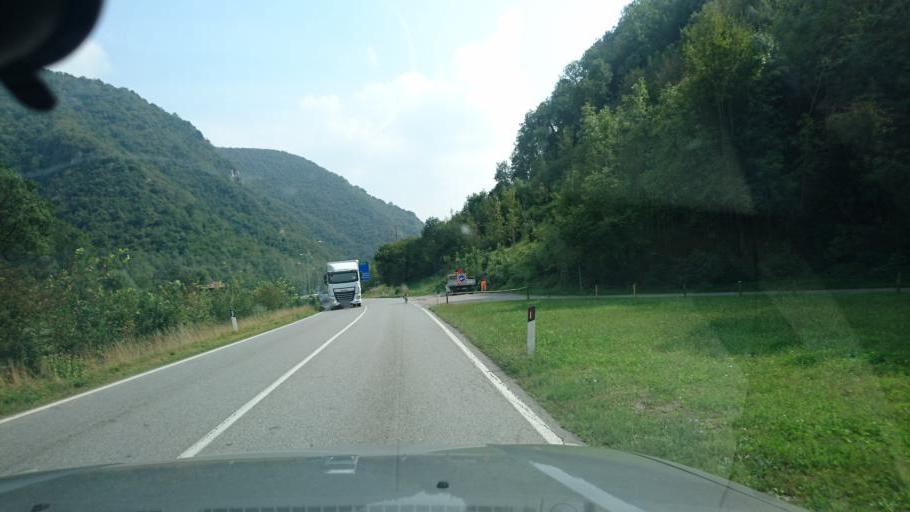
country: IT
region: Lombardy
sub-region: Provincia di Brescia
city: Vestone
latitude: 45.6911
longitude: 10.3963
